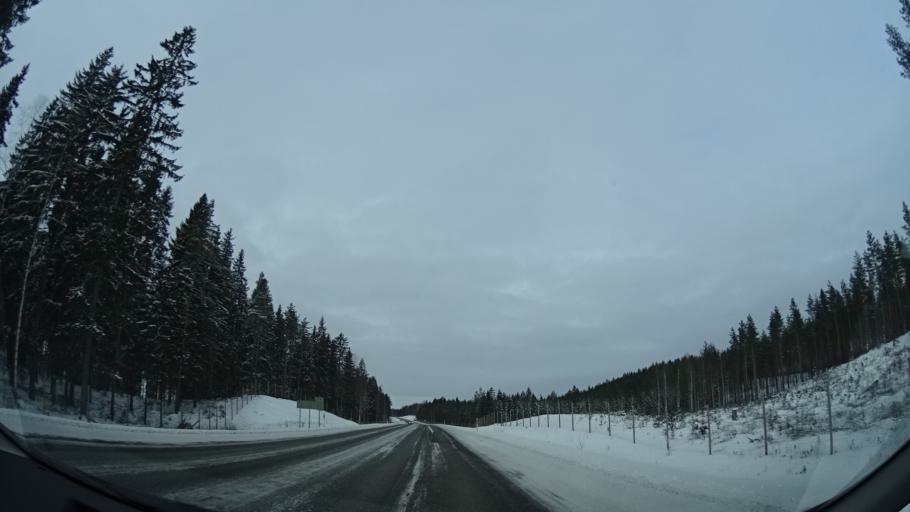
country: FI
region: Uusimaa
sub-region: Helsinki
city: Kaerkoelae
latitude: 60.6152
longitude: 24.0257
